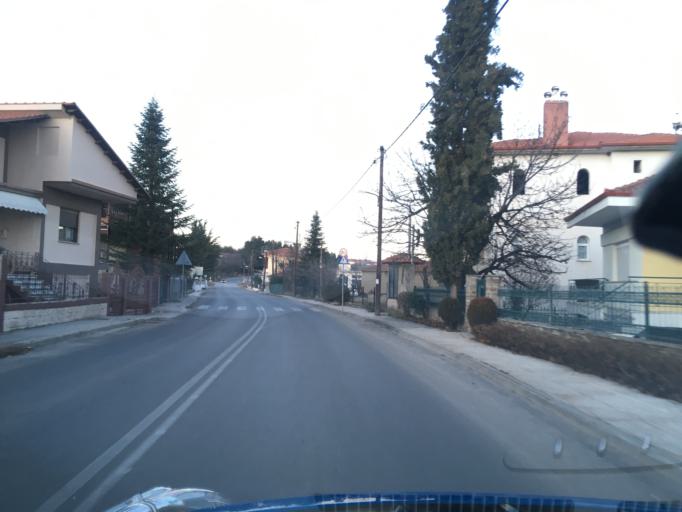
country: GR
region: West Macedonia
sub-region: Nomos Kozanis
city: Kozani
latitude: 40.2717
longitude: 21.7815
